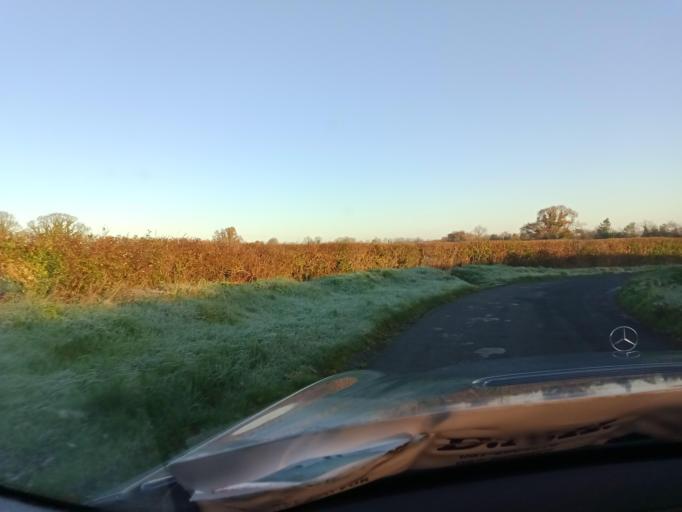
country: IE
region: Leinster
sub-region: Kilkenny
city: Callan
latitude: 52.5333
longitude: -7.4466
